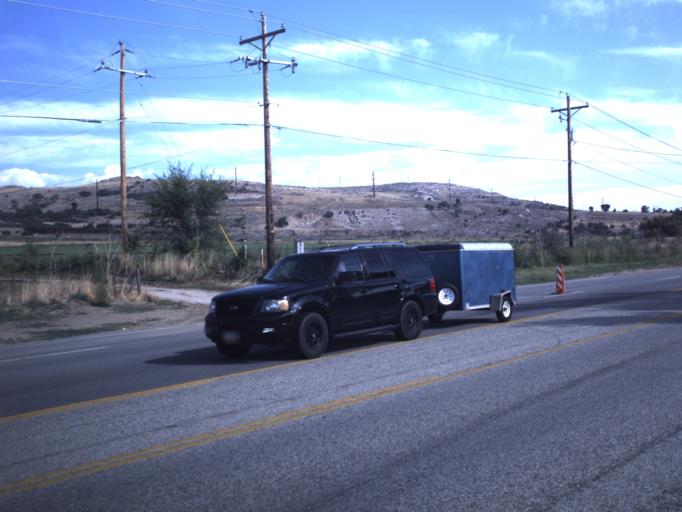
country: US
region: Utah
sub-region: Box Elder County
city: South Willard
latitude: 41.3648
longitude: -112.0356
